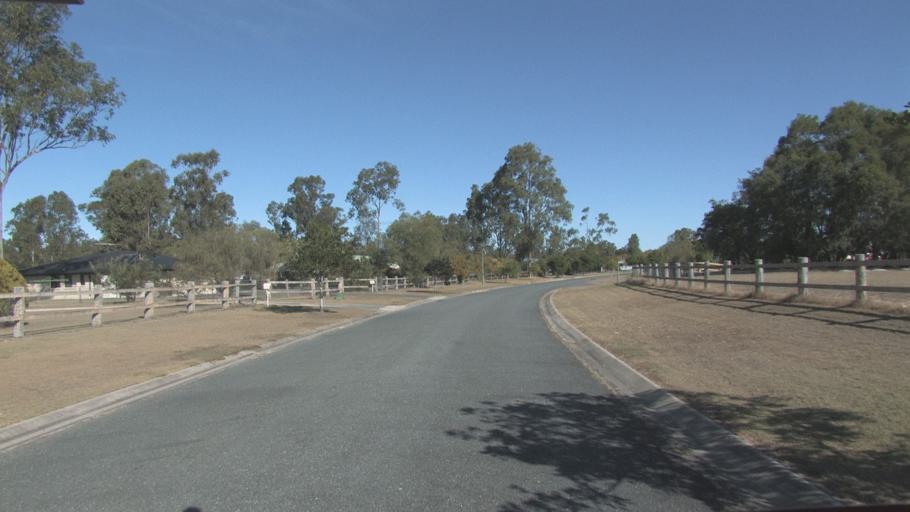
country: AU
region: Queensland
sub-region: Logan
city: North Maclean
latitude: -27.7995
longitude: 152.9693
